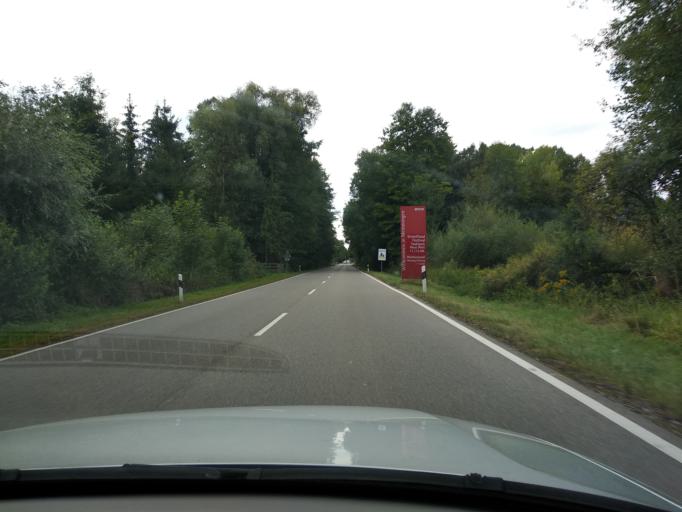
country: DE
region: Bavaria
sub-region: Swabia
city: Memmingen
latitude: 47.9795
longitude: 10.2023
